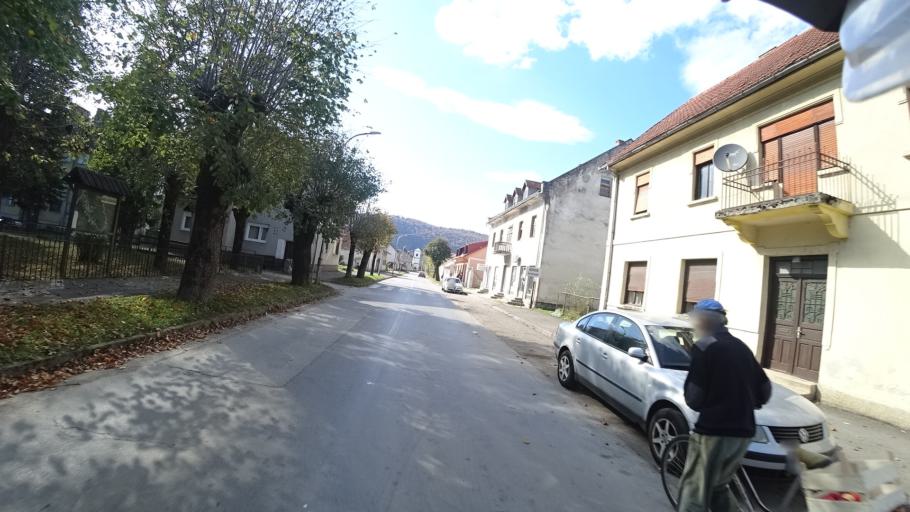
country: HR
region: Karlovacka
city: Plaski
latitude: 45.0819
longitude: 15.3630
